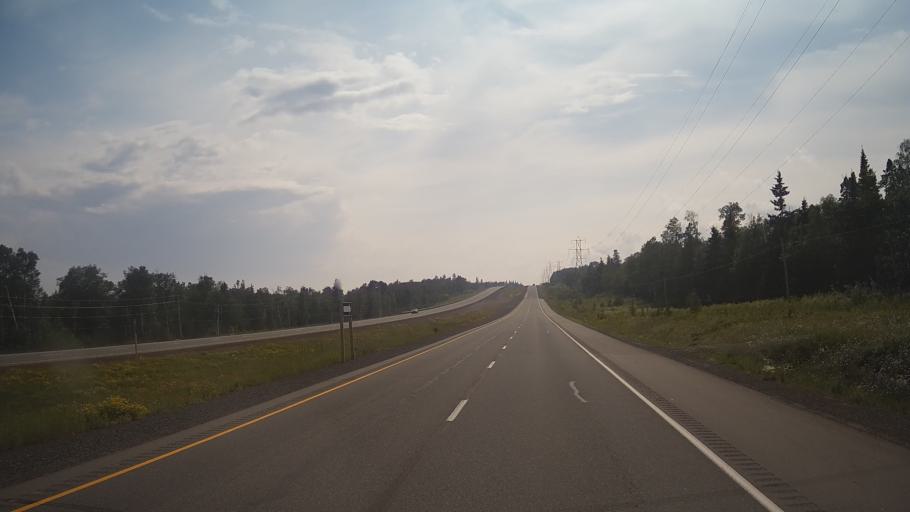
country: CA
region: Ontario
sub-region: Thunder Bay District
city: Thunder Bay
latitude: 48.5766
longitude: -88.8167
